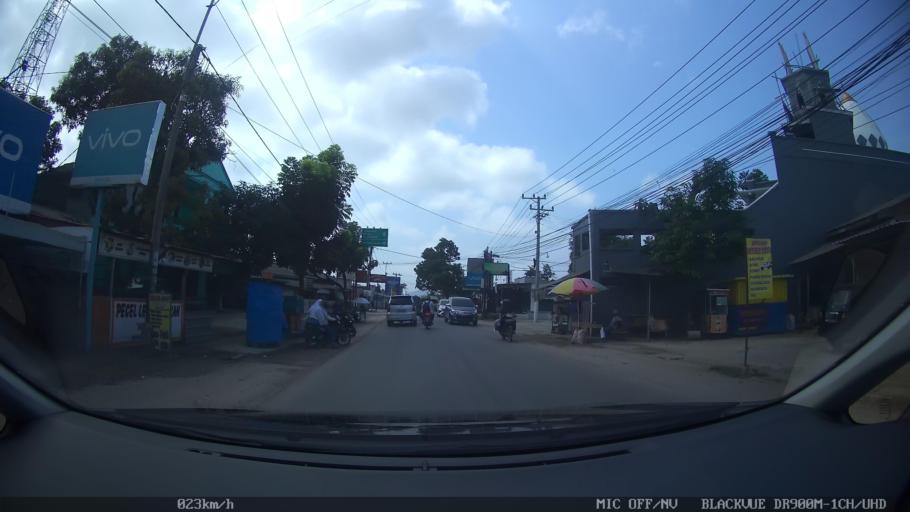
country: ID
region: Lampung
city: Kedaton
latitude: -5.3451
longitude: 105.2961
